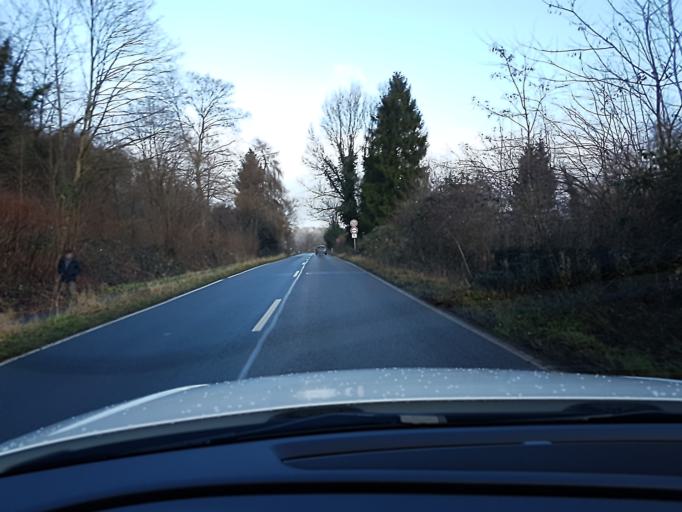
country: DE
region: North Rhine-Westphalia
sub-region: Regierungsbezirk Dusseldorf
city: Heiligenhaus
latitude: 51.3691
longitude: 6.9601
